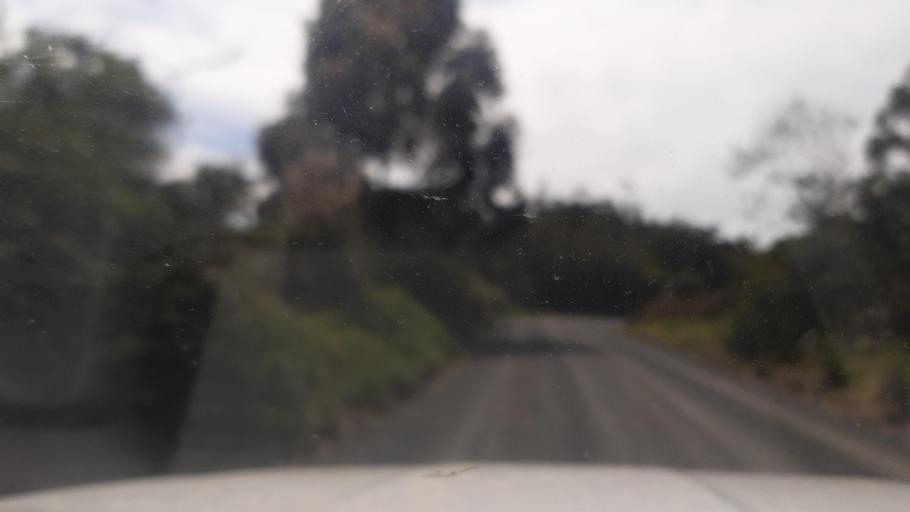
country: NZ
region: Northland
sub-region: Far North District
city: Kaitaia
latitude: -34.8364
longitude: 173.1231
